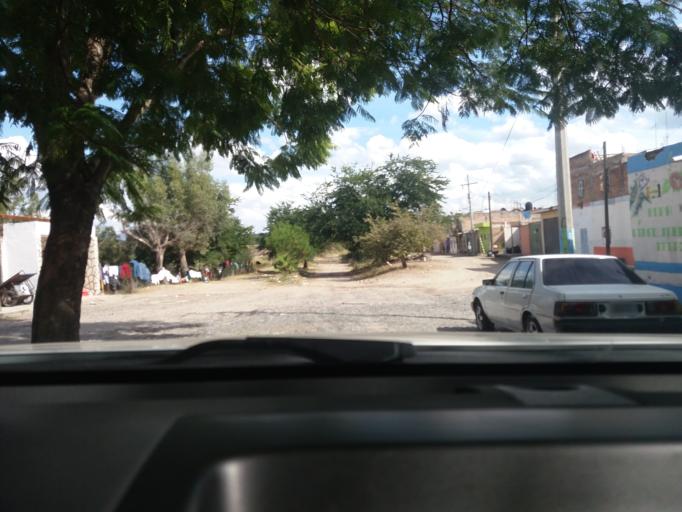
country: MX
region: Jalisco
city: Tala
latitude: 20.6567
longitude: -103.6939
